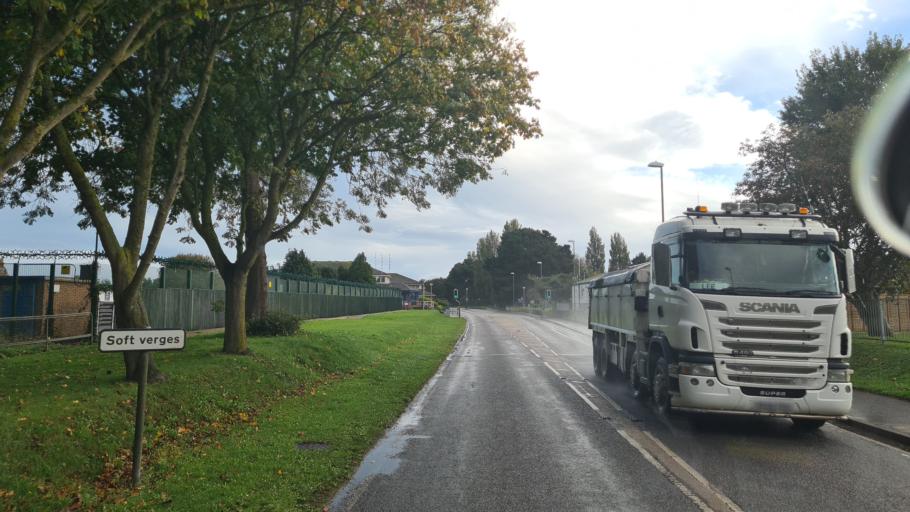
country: GB
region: England
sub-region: West Sussex
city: Littlehampton
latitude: 50.8175
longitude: -0.5801
